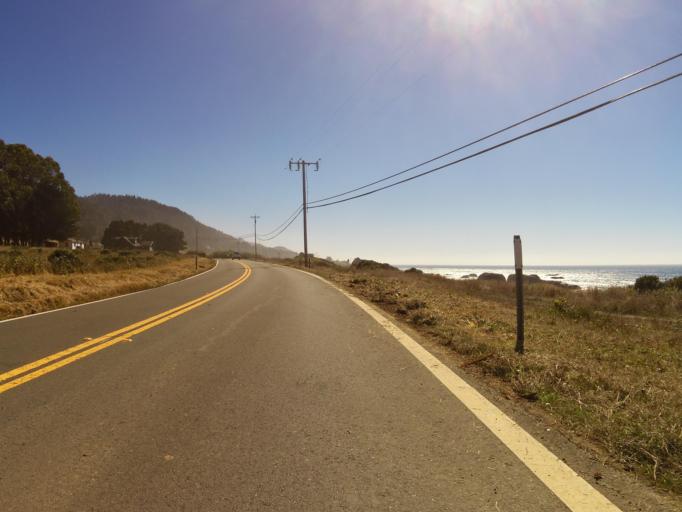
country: US
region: California
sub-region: Mendocino County
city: Fort Bragg
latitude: 39.6464
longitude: -123.7845
